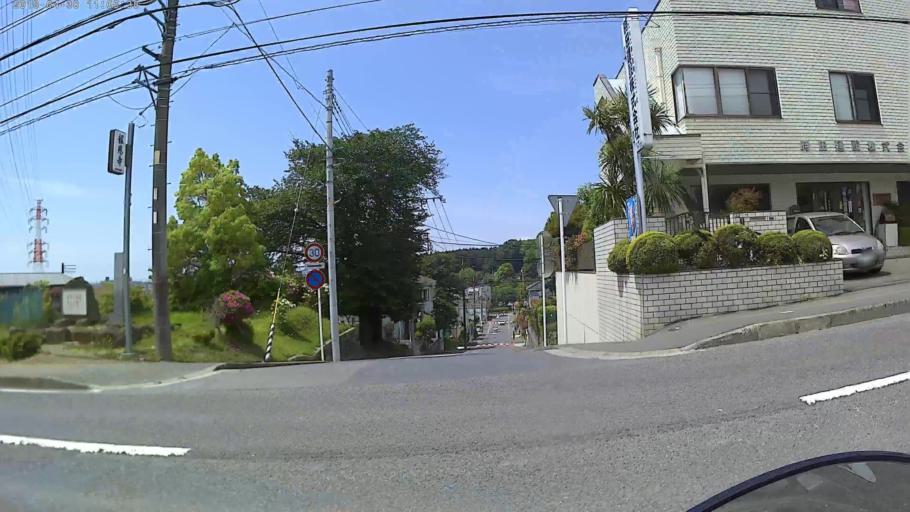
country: JP
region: Kanagawa
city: Minami-rinkan
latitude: 35.4511
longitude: 139.4298
